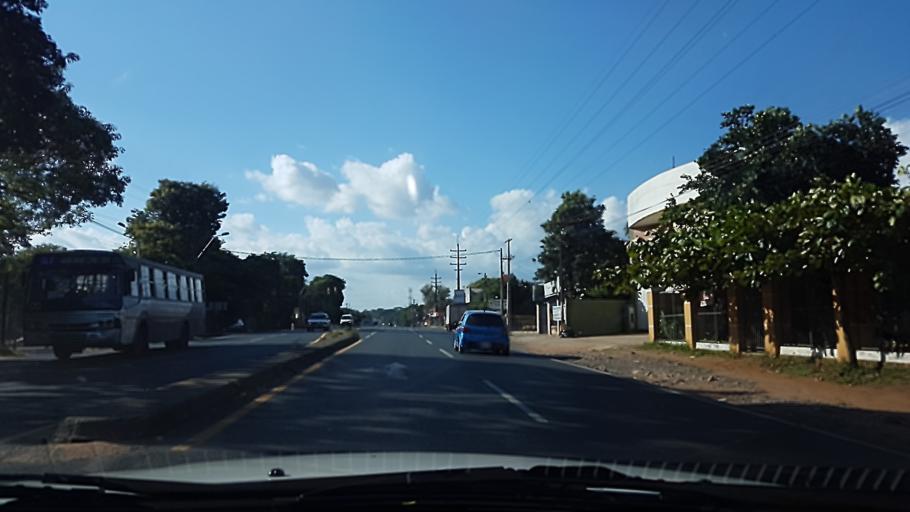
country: PY
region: Central
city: San Antonio
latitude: -25.4295
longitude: -57.5372
